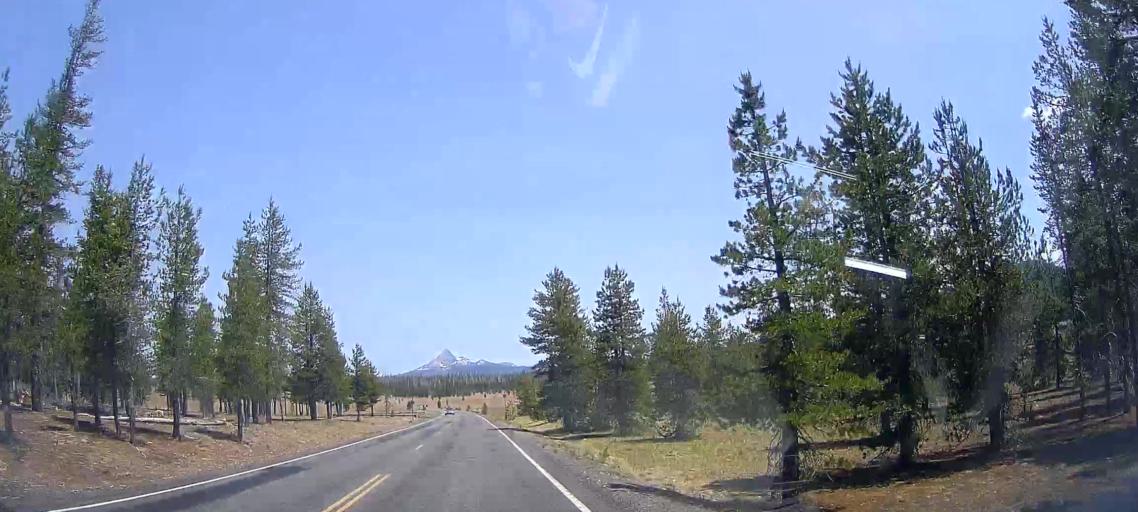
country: US
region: Oregon
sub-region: Lane County
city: Oakridge
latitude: 43.0267
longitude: -122.1196
